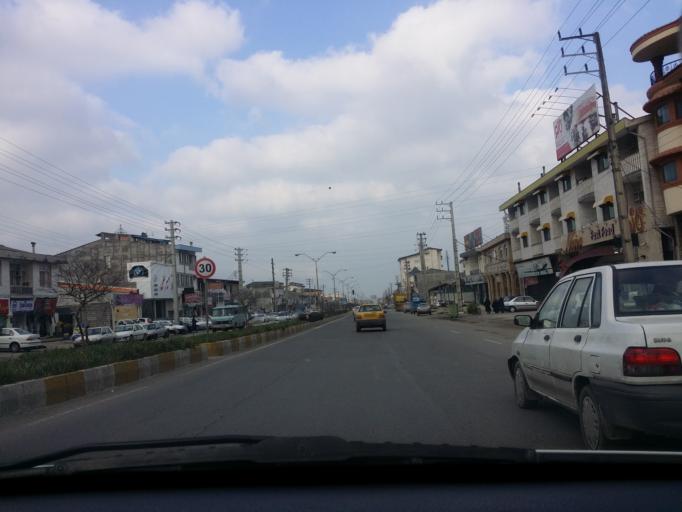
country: IR
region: Mazandaran
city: Chalus
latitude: 36.6702
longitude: 51.4077
